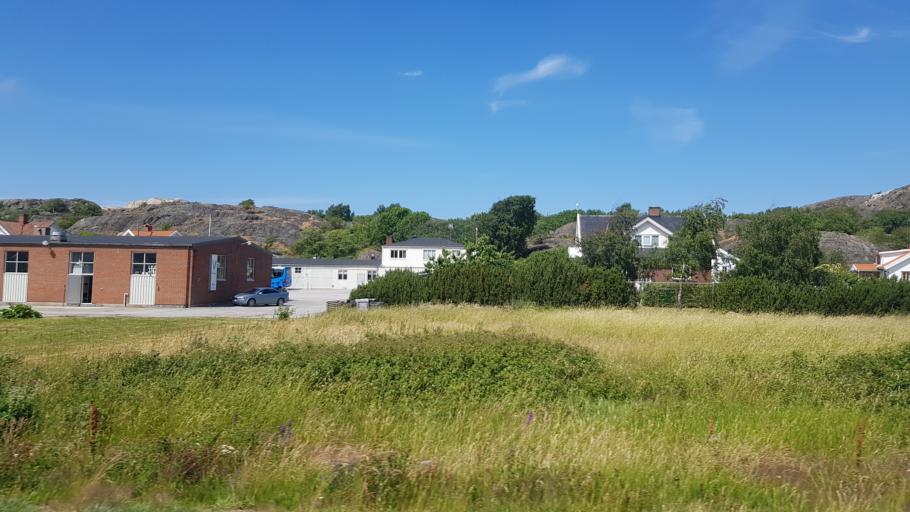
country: SE
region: Vaestra Goetaland
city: Ronnang
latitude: 57.9525
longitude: 11.5725
